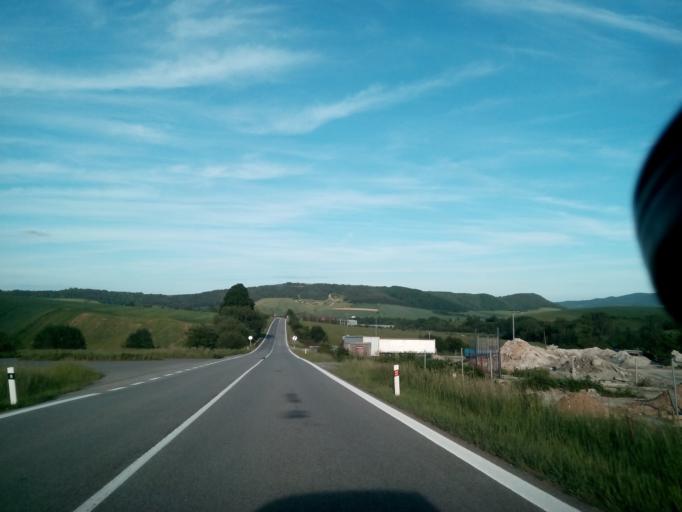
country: SK
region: Kosicky
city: Krompachy
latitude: 48.9948
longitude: 20.9141
